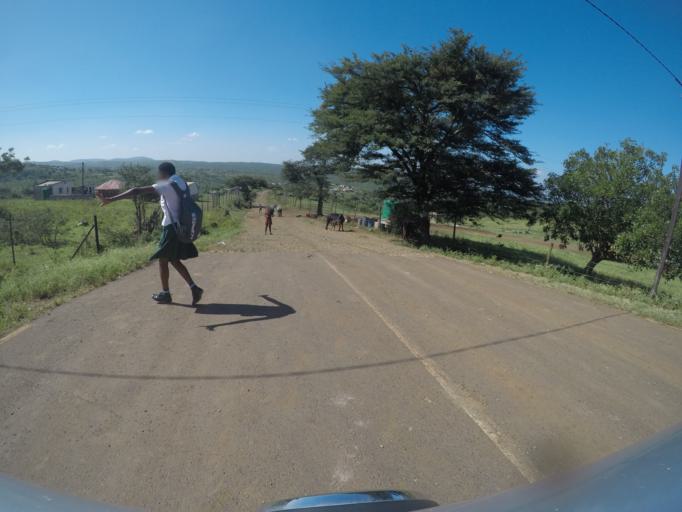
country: ZA
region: KwaZulu-Natal
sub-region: uThungulu District Municipality
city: Empangeni
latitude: -28.5622
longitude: 31.7035
